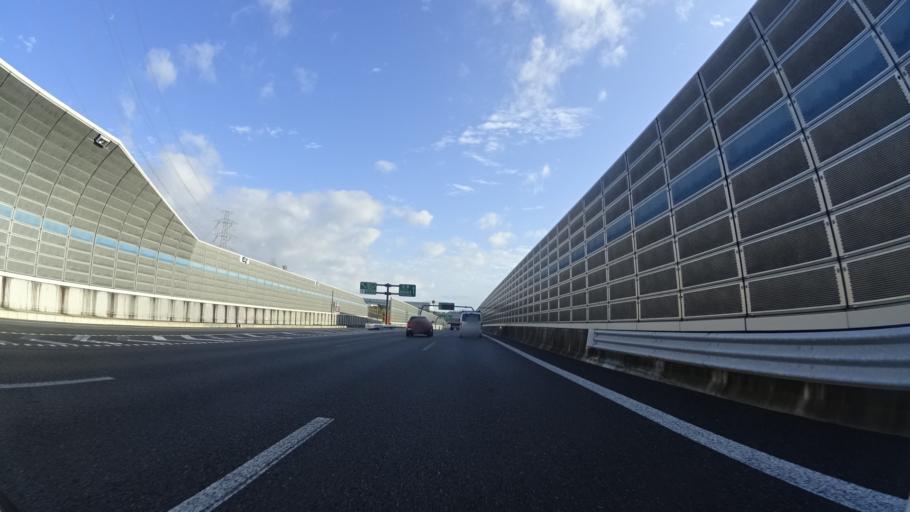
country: JP
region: Kyoto
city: Tanabe
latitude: 34.8064
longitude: 135.7101
